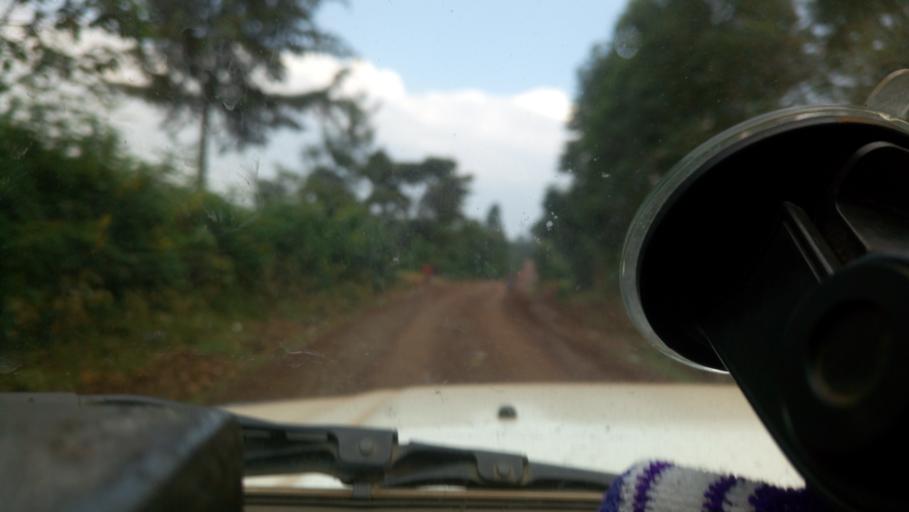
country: KE
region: Kericho
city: Sotik
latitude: -0.6415
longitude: 35.1574
